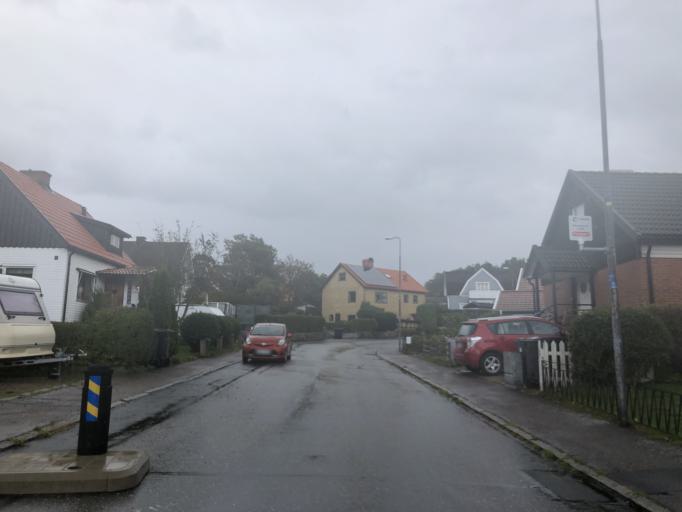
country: SE
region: Vaestra Goetaland
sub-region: Molndal
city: Moelndal
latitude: 57.6505
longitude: 12.0446
